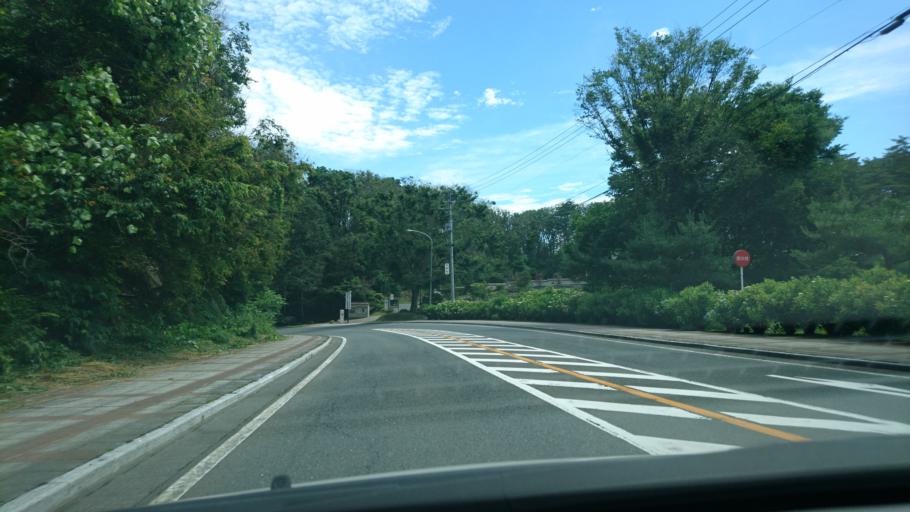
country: JP
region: Iwate
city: Hanamaki
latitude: 39.3994
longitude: 141.1669
